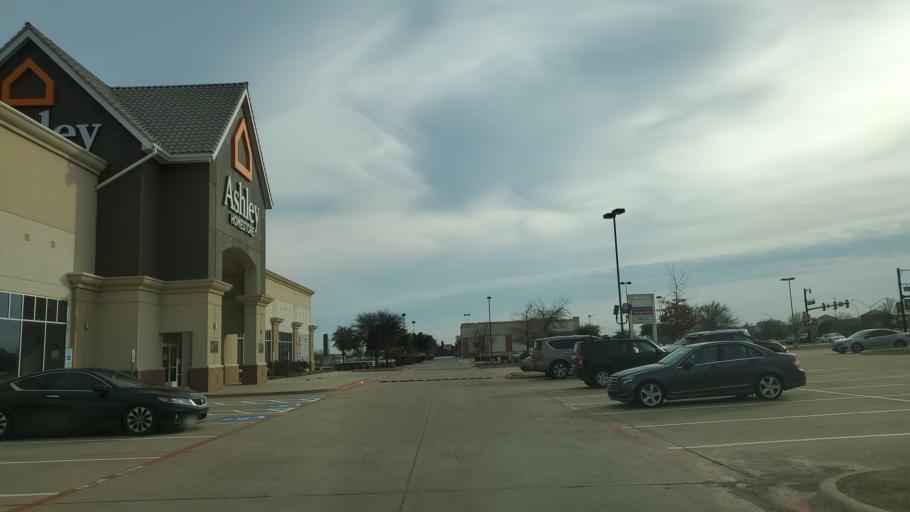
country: US
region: Texas
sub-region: Dallas County
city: Coppell
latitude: 32.9710
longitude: -97.0358
